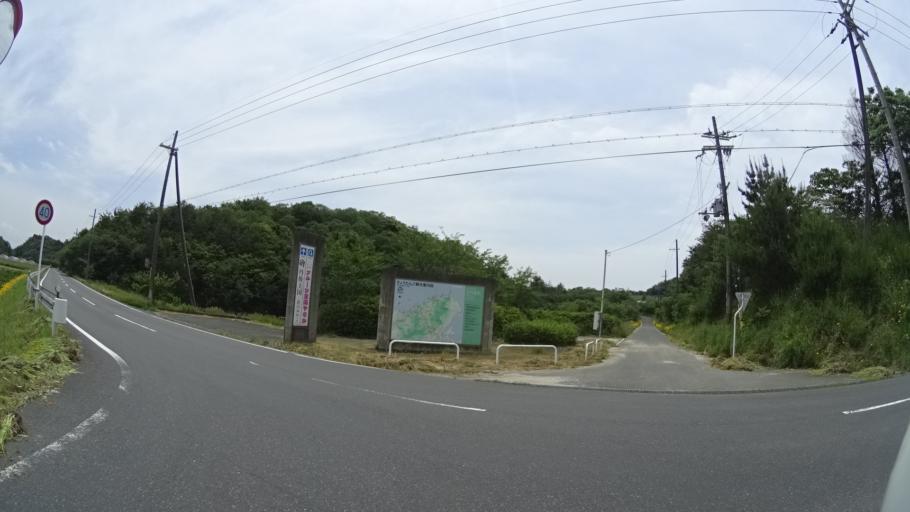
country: JP
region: Kyoto
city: Miyazu
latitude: 35.6791
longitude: 135.0656
